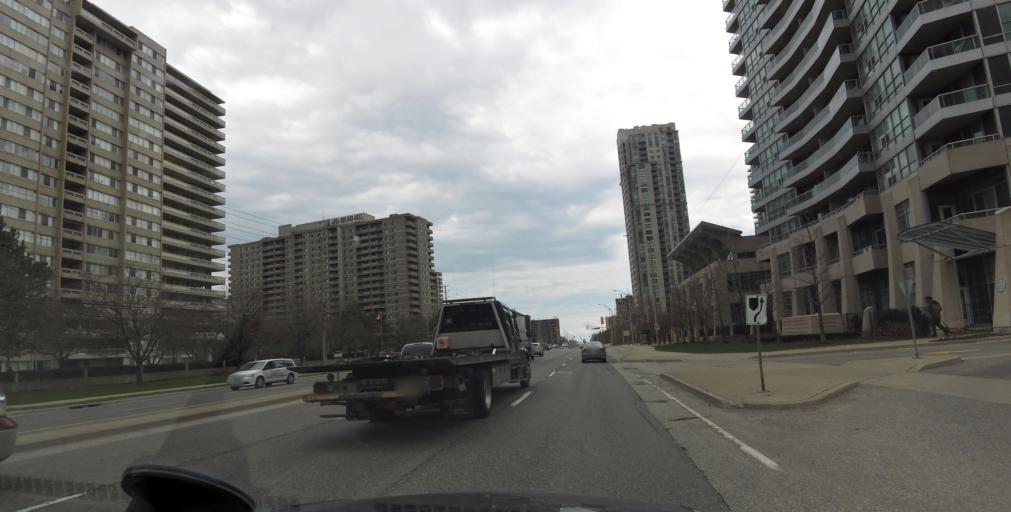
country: CA
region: Ontario
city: Mississauga
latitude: 43.5915
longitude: -79.6325
